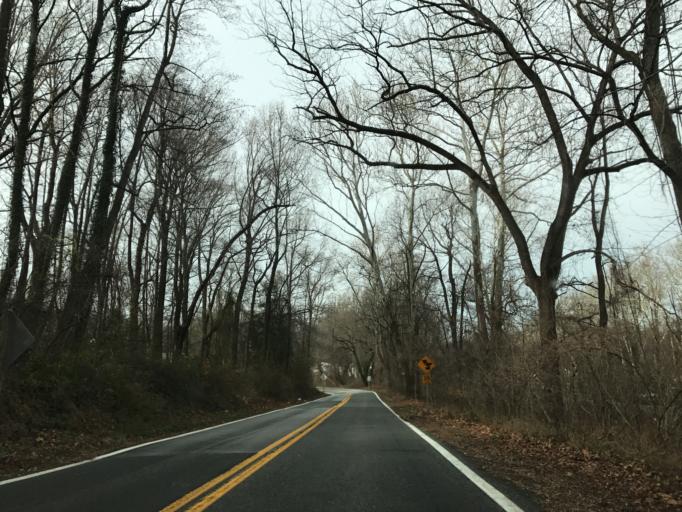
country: US
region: Maryland
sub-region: Anne Arundel County
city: Arnold
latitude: 39.0339
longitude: -76.5084
